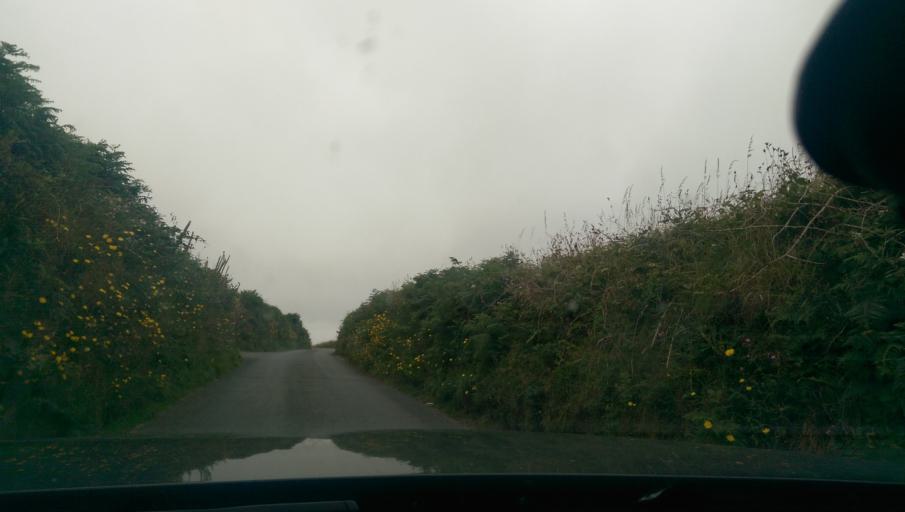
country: GB
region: England
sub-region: Cornwall
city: St. Buryan
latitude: 50.0972
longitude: -5.6512
